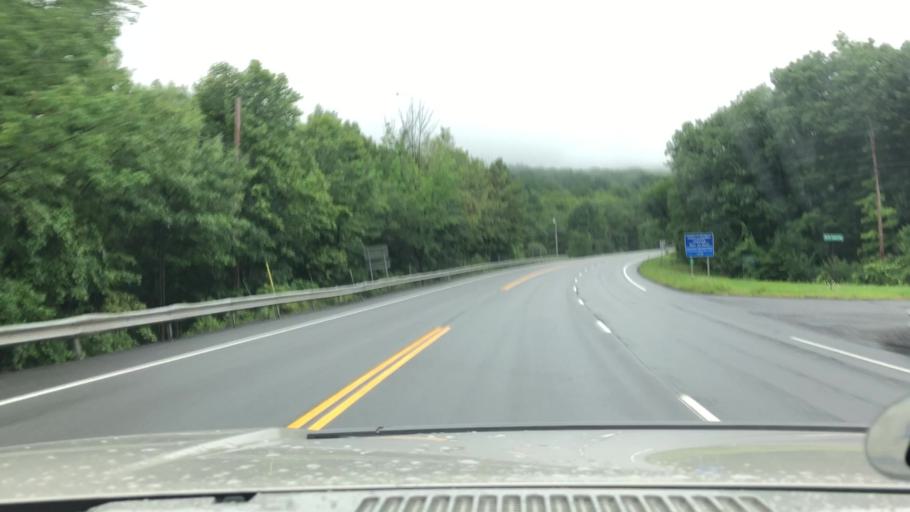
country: US
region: New York
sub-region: Greene County
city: Cairo
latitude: 42.3264
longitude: -74.1105
